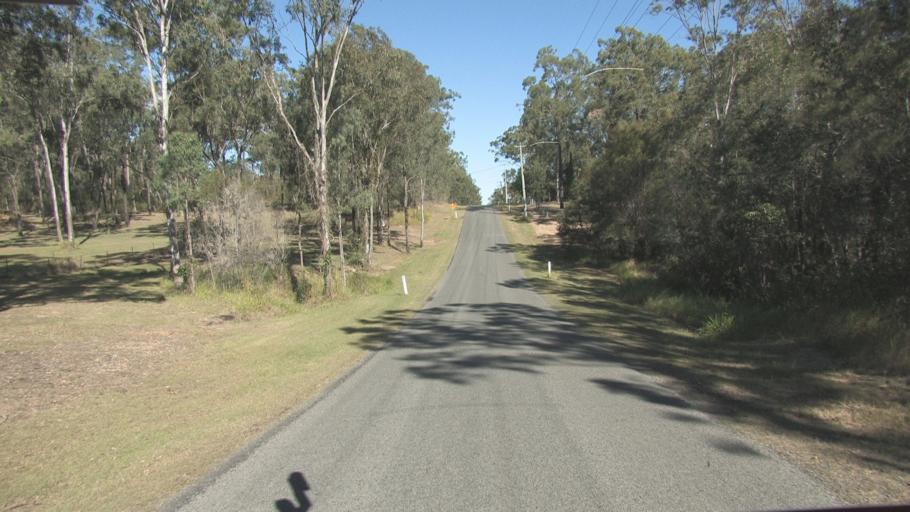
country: AU
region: Queensland
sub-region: Logan
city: Chambers Flat
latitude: -27.8085
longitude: 153.0788
